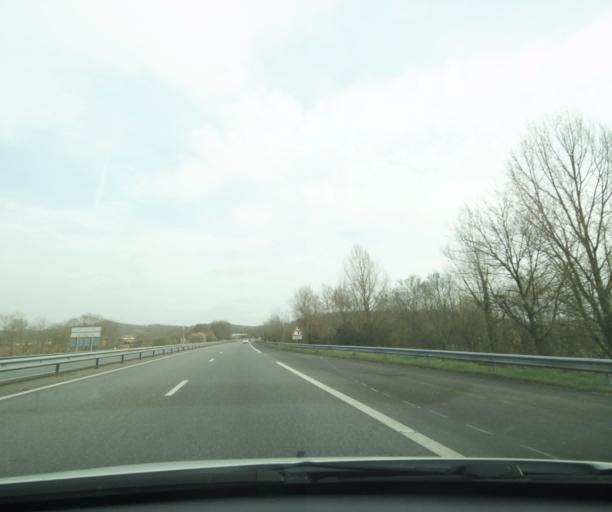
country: FR
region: Aquitaine
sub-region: Departement des Landes
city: Labatut
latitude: 43.5078
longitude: -1.0277
